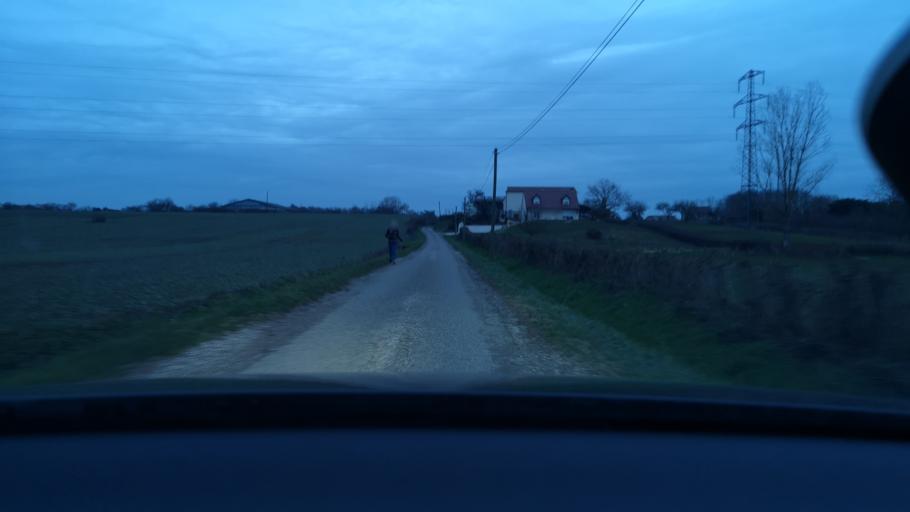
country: FR
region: Bourgogne
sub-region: Departement de Saone-et-Loire
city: Saint-Remy
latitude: 46.7653
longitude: 4.8103
